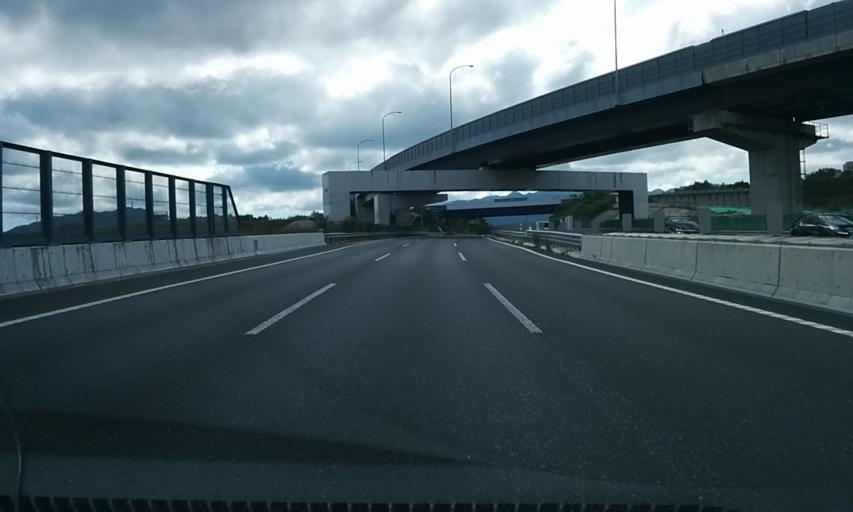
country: JP
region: Hyogo
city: Sandacho
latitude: 34.8498
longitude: 135.2227
